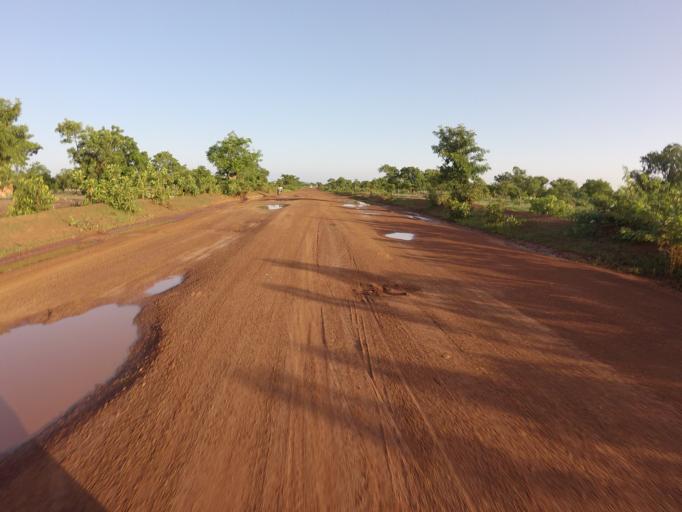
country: TG
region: Savanes
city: Sansanne-Mango
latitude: 10.2743
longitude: -0.0826
